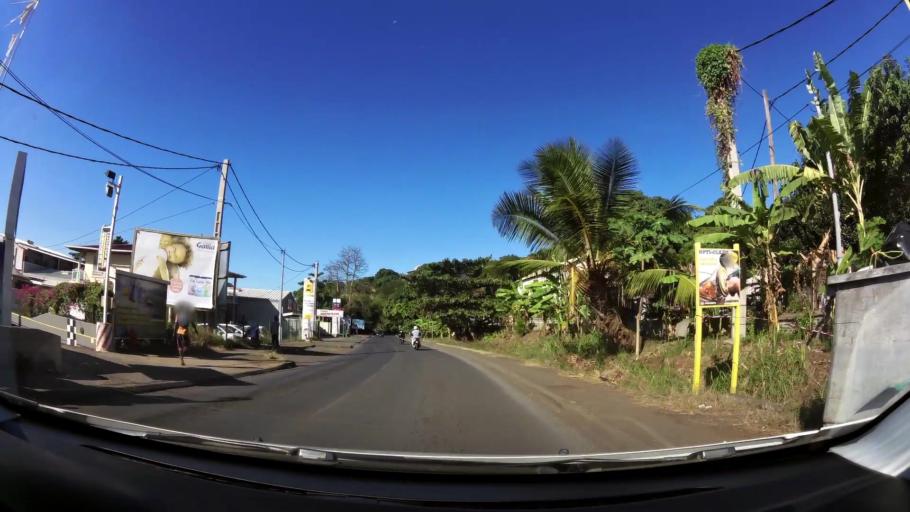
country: YT
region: Mamoudzou
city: Mamoudzou
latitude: -12.7759
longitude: 45.2260
